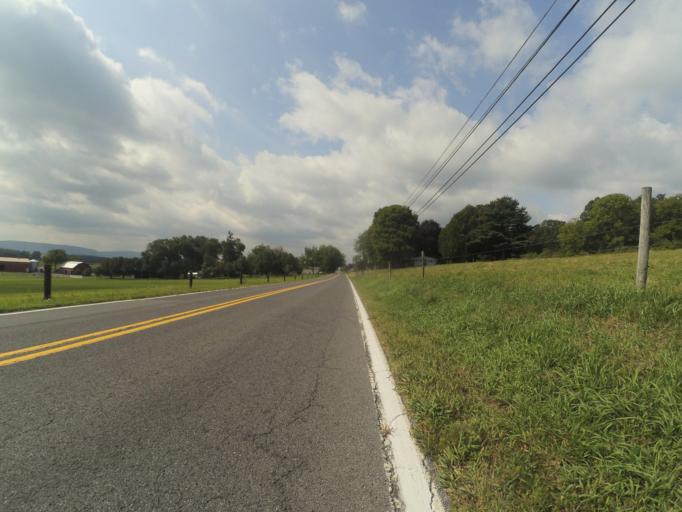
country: US
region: Pennsylvania
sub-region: Centre County
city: Bellefonte
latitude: 40.9342
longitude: -77.7424
